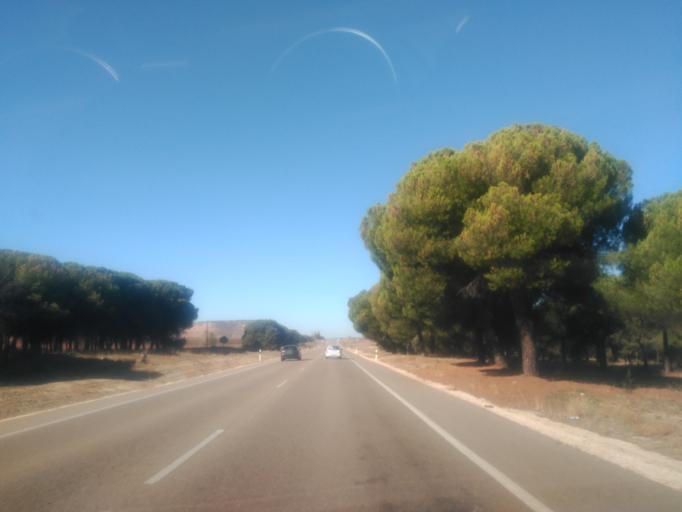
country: ES
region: Castille and Leon
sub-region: Provincia de Valladolid
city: Manzanillo
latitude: 41.6138
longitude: -4.1816
